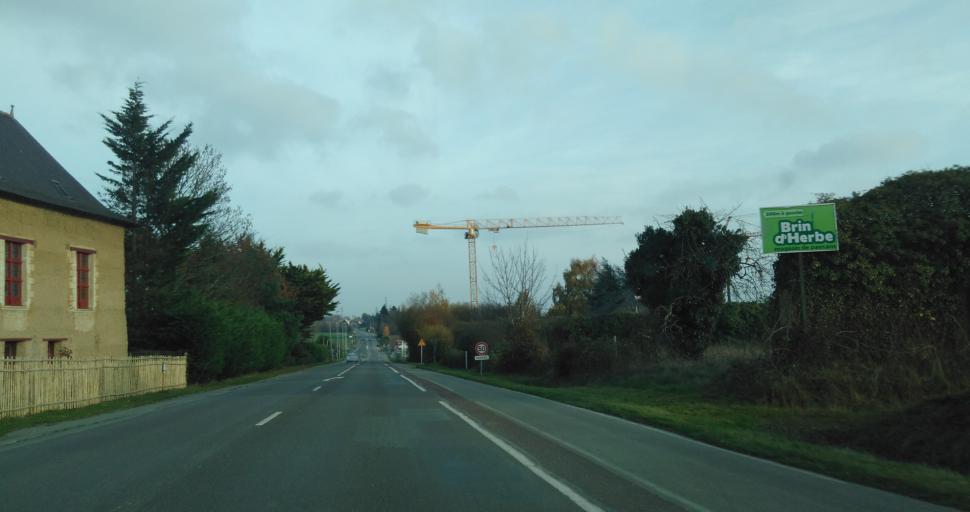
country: FR
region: Brittany
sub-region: Departement d'Ille-et-Vilaine
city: Vezin-le-Coquet
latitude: 48.1188
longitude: -1.7468
